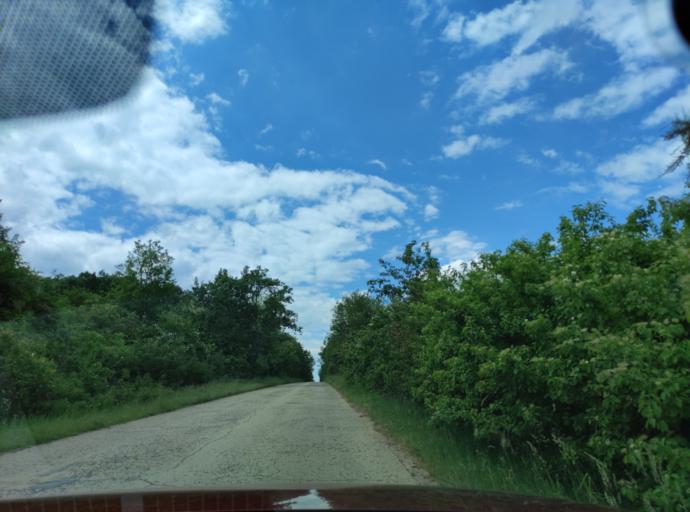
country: BG
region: Montana
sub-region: Obshtina Berkovitsa
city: Berkovitsa
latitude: 43.3581
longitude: 23.0931
